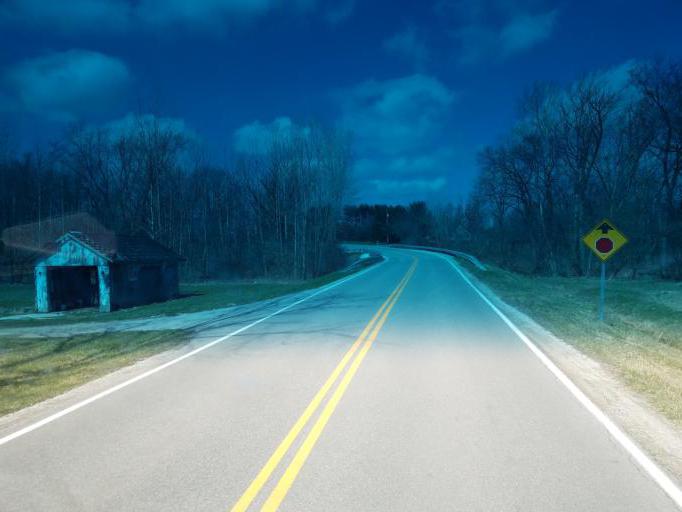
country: US
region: Ohio
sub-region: Crawford County
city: Bucyrus
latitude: 40.8035
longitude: -83.0052
